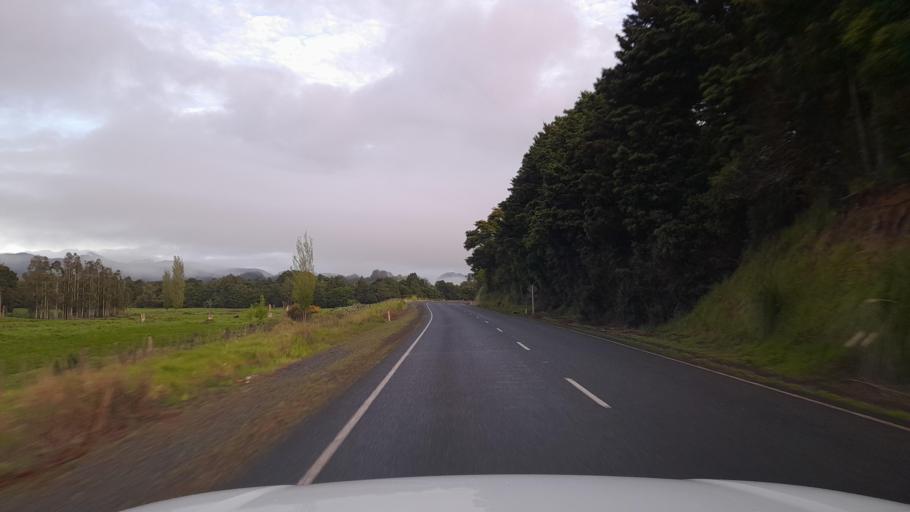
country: NZ
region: Northland
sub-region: Kaipara District
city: Dargaville
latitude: -35.7144
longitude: 173.9471
